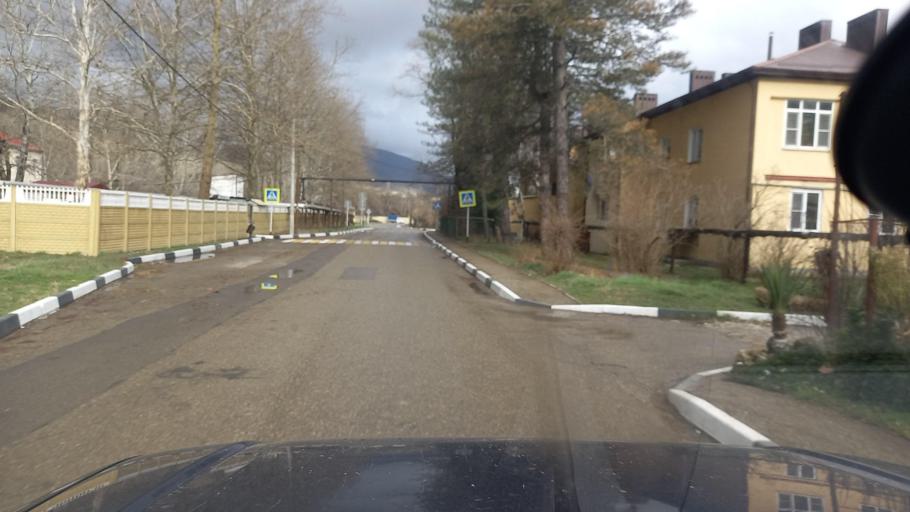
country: RU
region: Krasnodarskiy
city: Pshada
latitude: 44.4759
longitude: 38.3991
